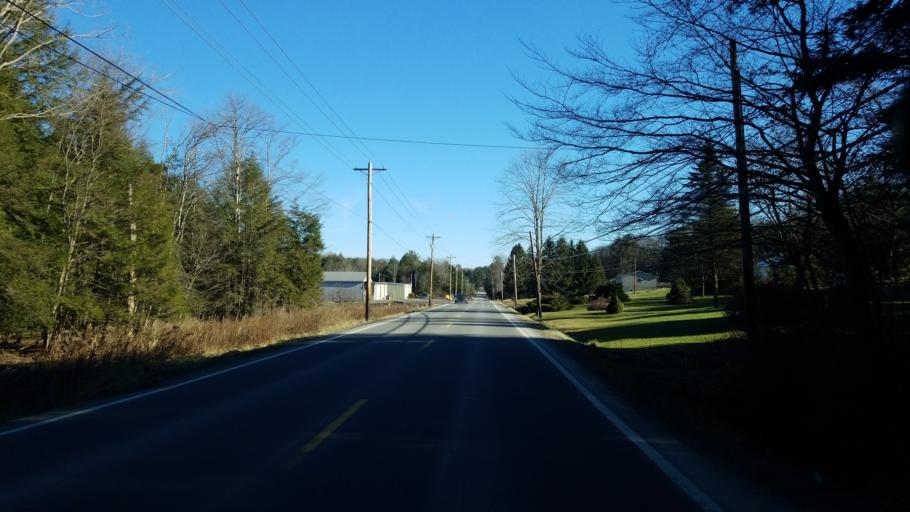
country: US
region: Pennsylvania
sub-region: Jefferson County
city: Falls Creek
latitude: 41.1774
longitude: -78.8523
